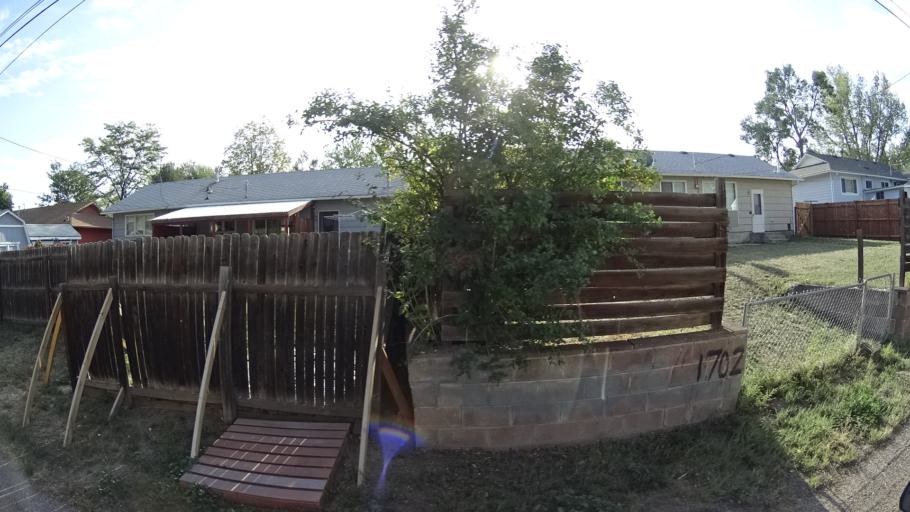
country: US
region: Colorado
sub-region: El Paso County
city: Colorado Springs
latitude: 38.8576
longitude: -104.7692
